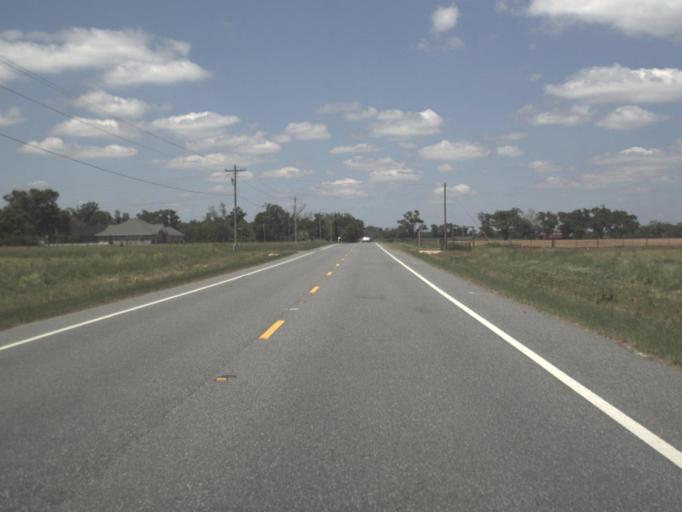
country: US
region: Florida
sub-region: Santa Rosa County
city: Point Baker
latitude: 30.8192
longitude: -87.0458
